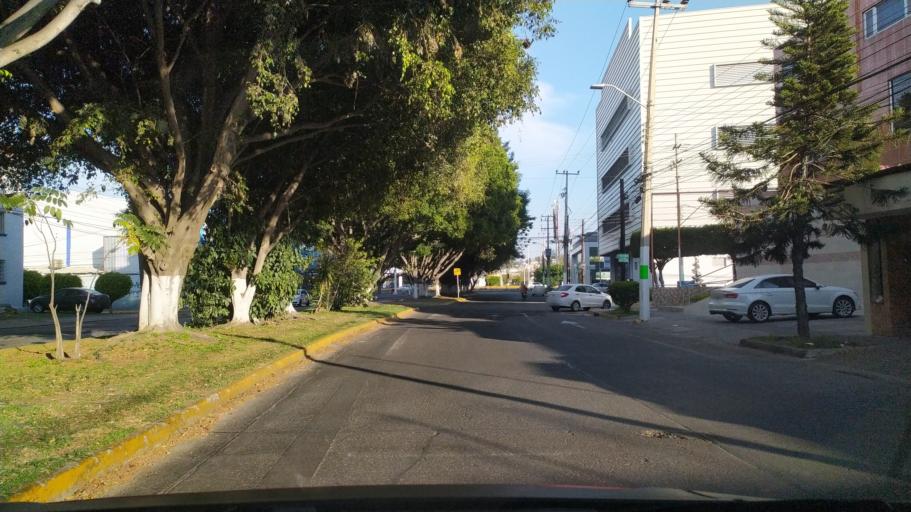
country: MX
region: Jalisco
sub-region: Tlajomulco de Zuniga
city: La Tijera
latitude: 20.6260
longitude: -103.4212
